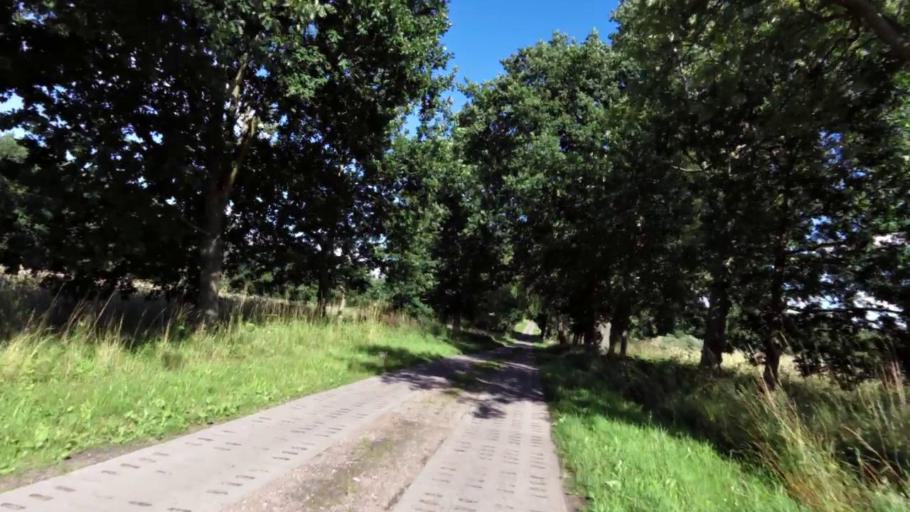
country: PL
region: West Pomeranian Voivodeship
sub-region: Powiat slawienski
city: Slawno
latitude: 54.4634
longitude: 16.7181
